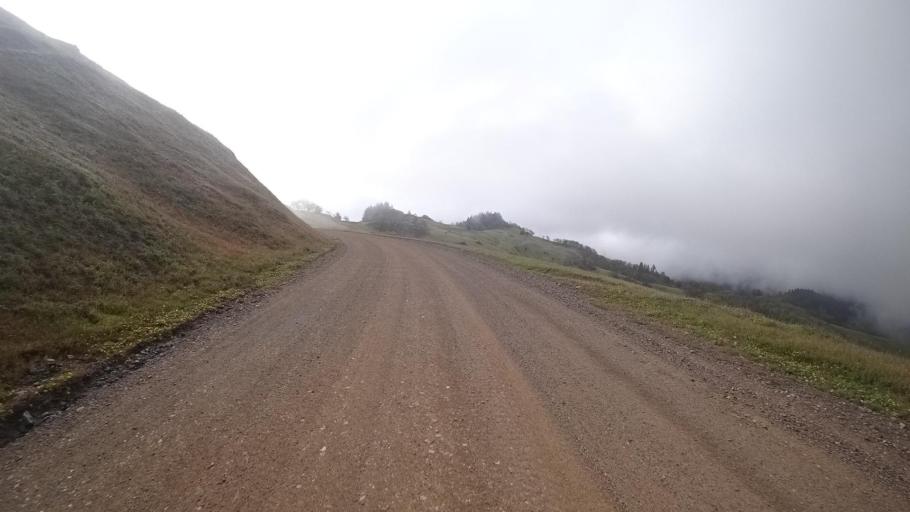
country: US
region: California
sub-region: Humboldt County
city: Redway
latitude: 40.2003
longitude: -123.7111
